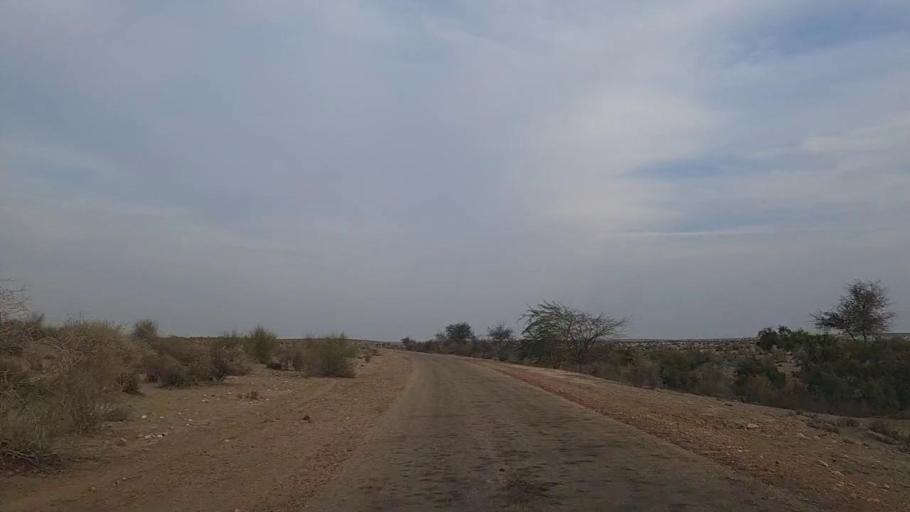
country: PK
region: Sindh
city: Daur
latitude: 26.4939
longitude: 68.5314
